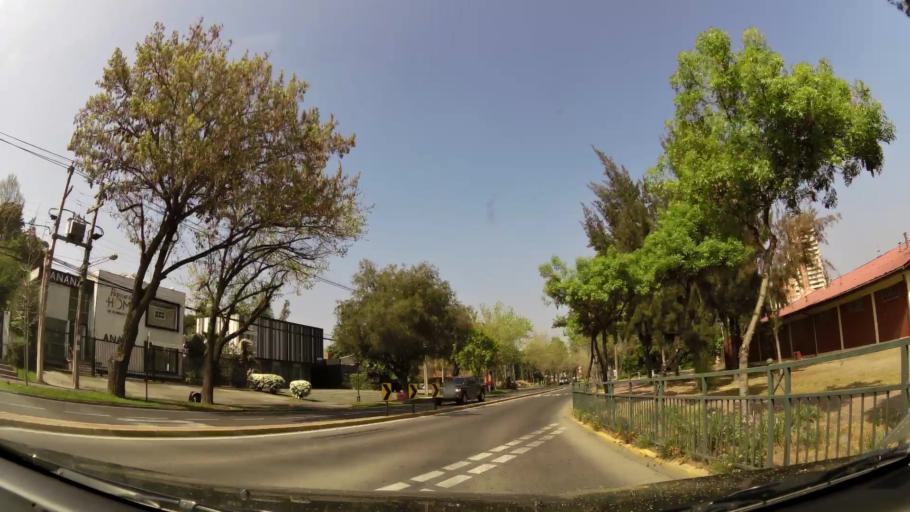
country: CL
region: Santiago Metropolitan
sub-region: Provincia de Santiago
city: Villa Presidente Frei, Nunoa, Santiago, Chile
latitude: -33.3927
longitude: -70.5970
